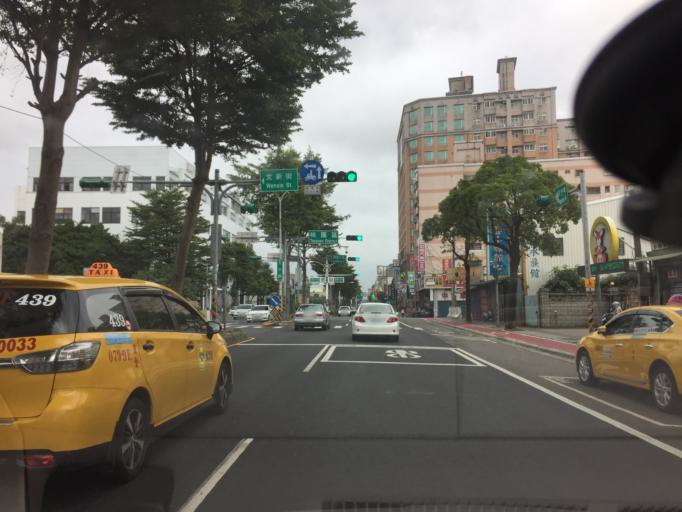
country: TW
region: Taiwan
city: Taoyuan City
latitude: 24.9927
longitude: 121.2738
